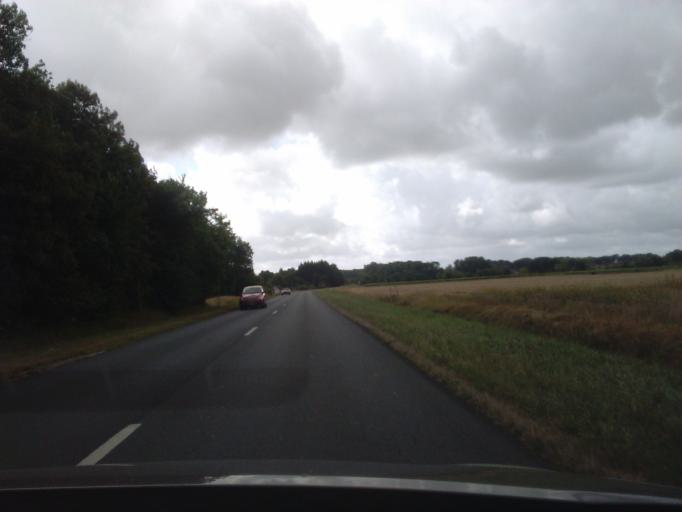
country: FR
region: Centre
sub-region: Departement du Loir-et-Cher
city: Cormeray
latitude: 47.5069
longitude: 1.4038
